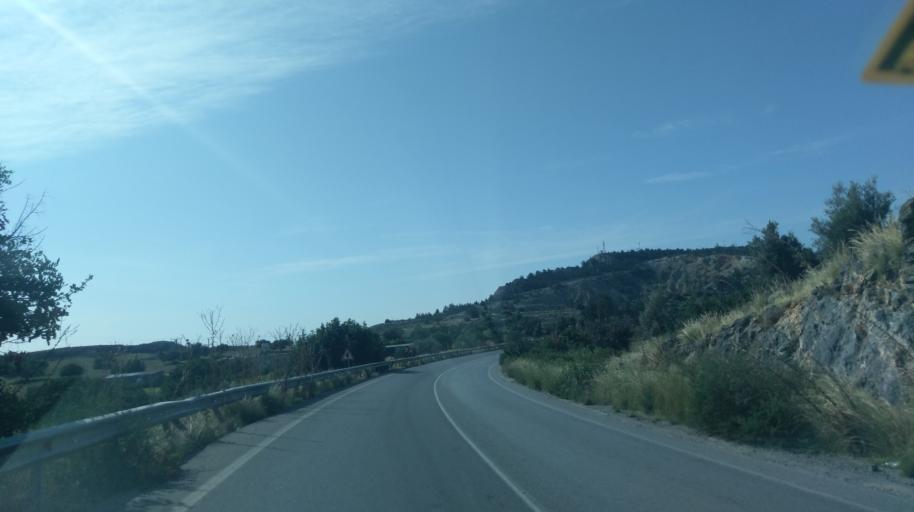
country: CY
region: Lefkosia
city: Nicosia
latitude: 35.2711
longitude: 33.4870
